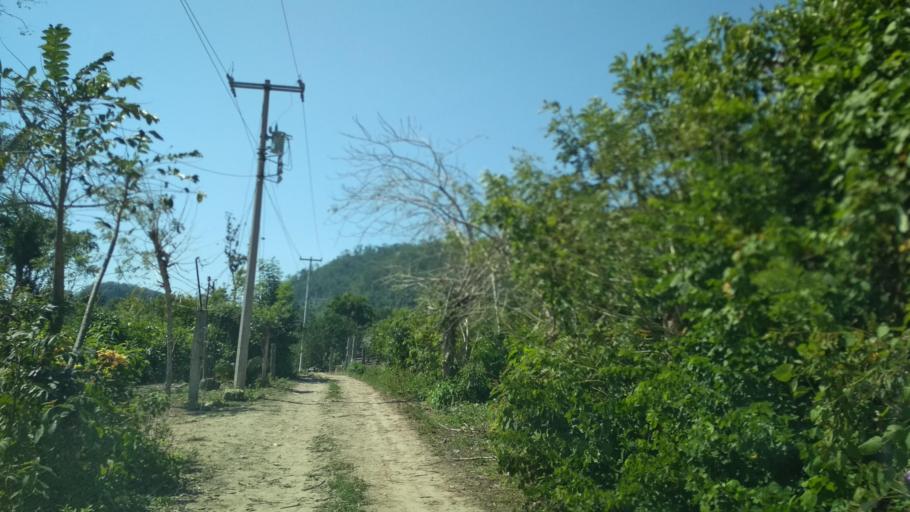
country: MX
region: Veracruz
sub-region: Papantla
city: Polutla
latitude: 20.4714
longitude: -97.2222
